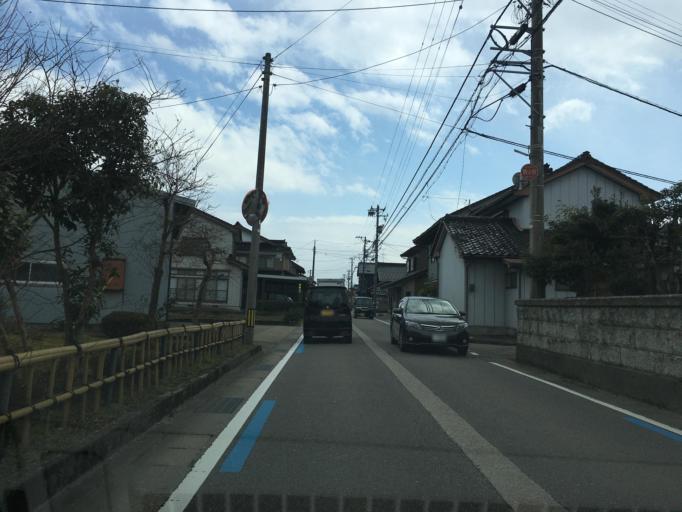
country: JP
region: Toyama
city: Kuragaki-kosugi
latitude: 36.6862
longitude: 137.1188
